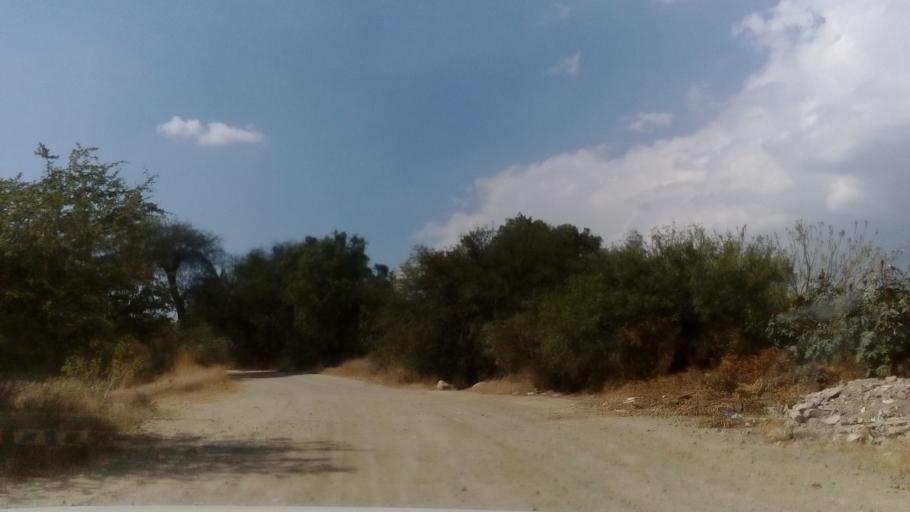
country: MX
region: Guanajuato
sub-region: Silao de la Victoria
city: San Francisco (Banos de Agua Caliente)
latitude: 21.0718
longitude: -101.4624
